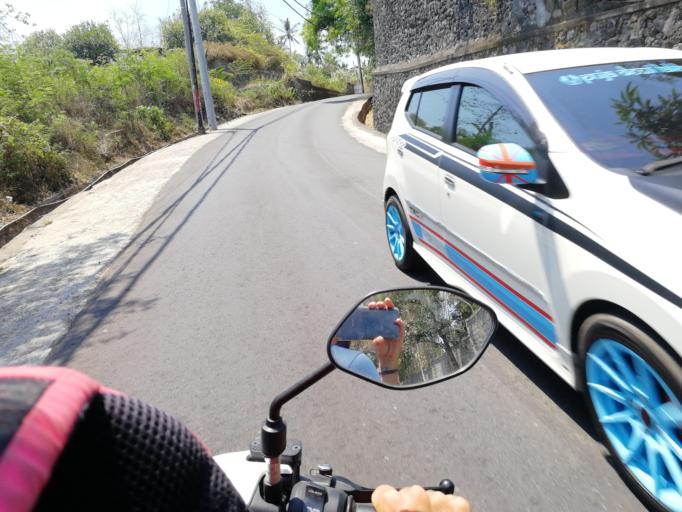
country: ID
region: Bali
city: Banjar Timbrah
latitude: -8.4836
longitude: 115.5994
